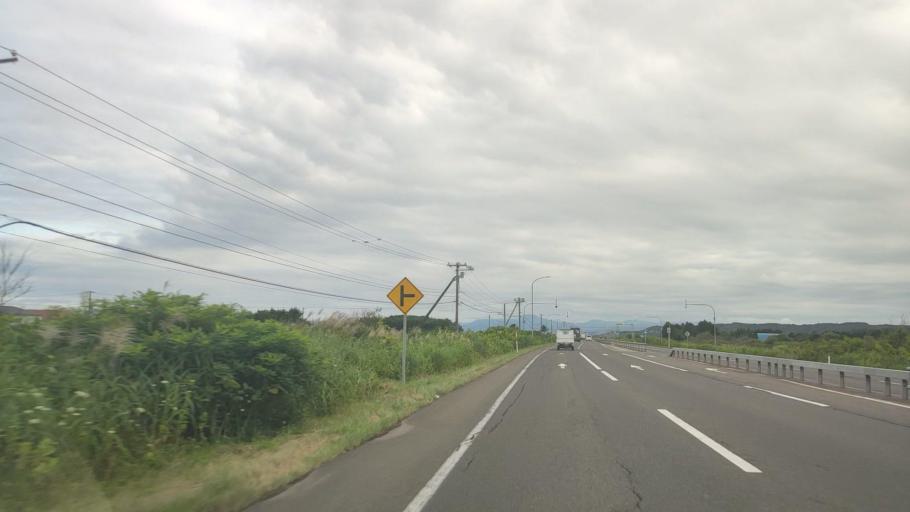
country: JP
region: Hokkaido
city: Niseko Town
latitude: 42.4091
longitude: 140.3064
